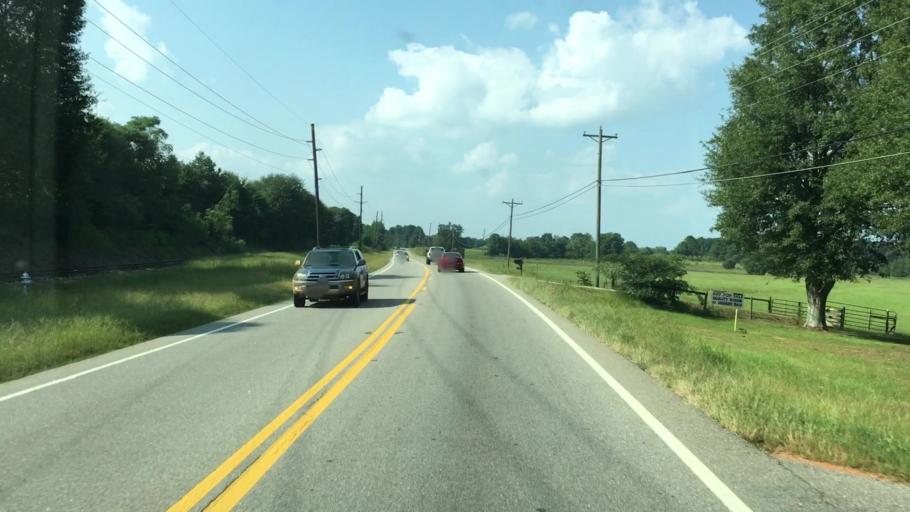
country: US
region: Georgia
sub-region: Walton County
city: Social Circle
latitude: 33.6988
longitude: -83.7015
